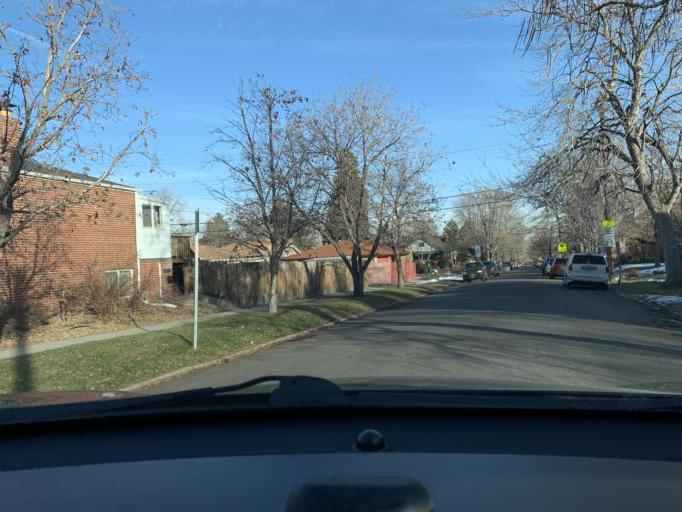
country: US
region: Colorado
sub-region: Adams County
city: Berkley
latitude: 39.7732
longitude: -105.0345
